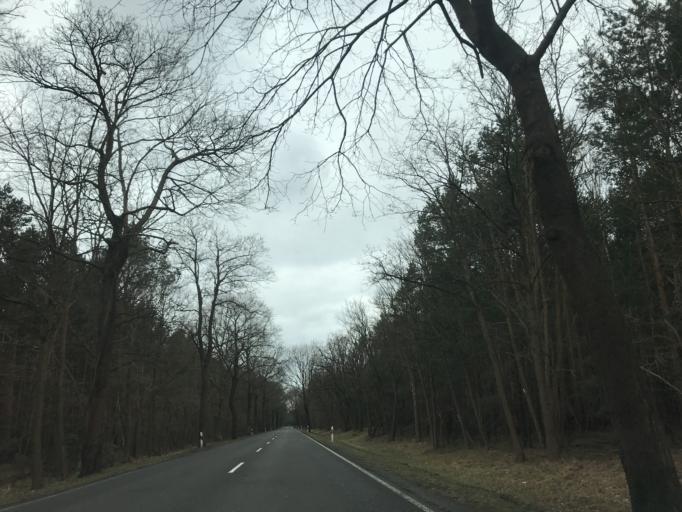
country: DE
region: Brandenburg
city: Kasel-Golzig
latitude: 51.9732
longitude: 13.6588
